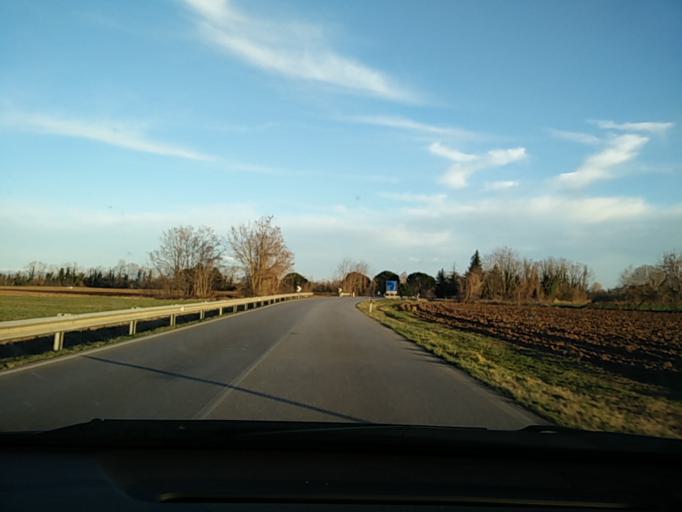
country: IT
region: Friuli Venezia Giulia
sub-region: Provincia di Udine
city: Lestizza
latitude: 45.9917
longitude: 13.1299
